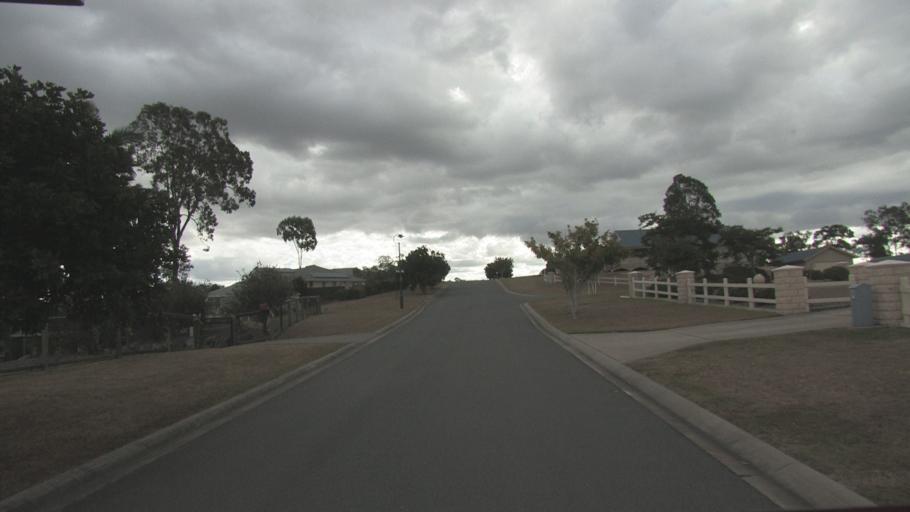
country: AU
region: Queensland
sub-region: Logan
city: Cedar Vale
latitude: -27.8687
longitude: 153.0806
